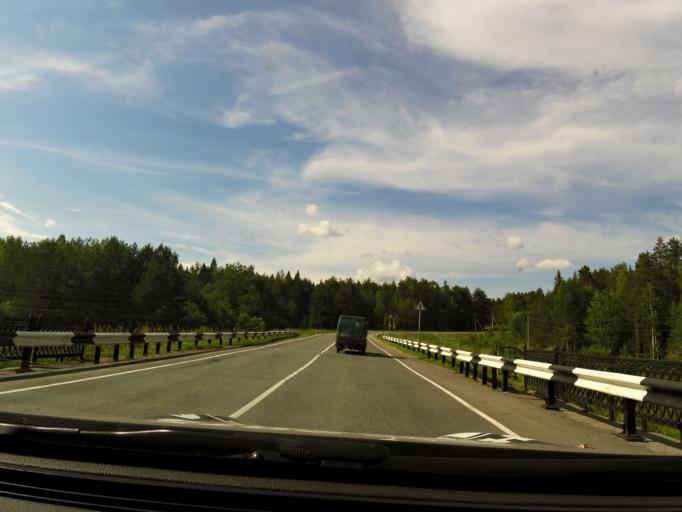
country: RU
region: Kirov
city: Belaya Kholunitsa
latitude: 58.8366
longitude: 50.6881
